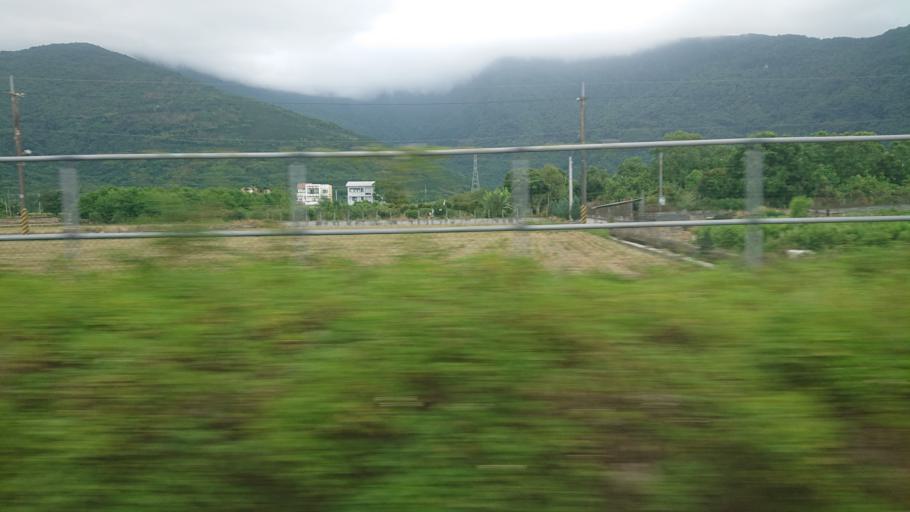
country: TW
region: Taiwan
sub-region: Hualien
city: Hualian
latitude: 23.7440
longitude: 121.4457
